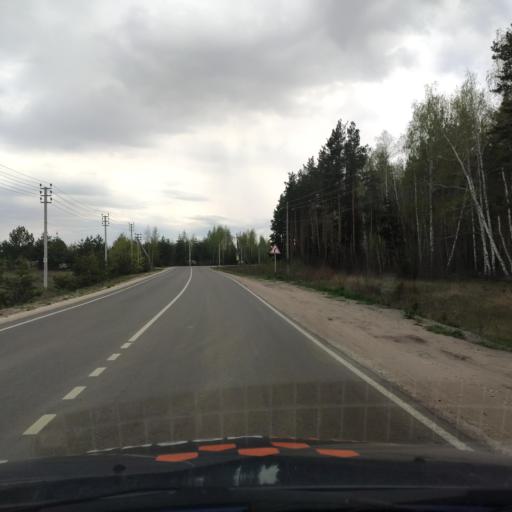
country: RU
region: Voronezj
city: Podgornoye
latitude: 51.8669
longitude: 39.1712
